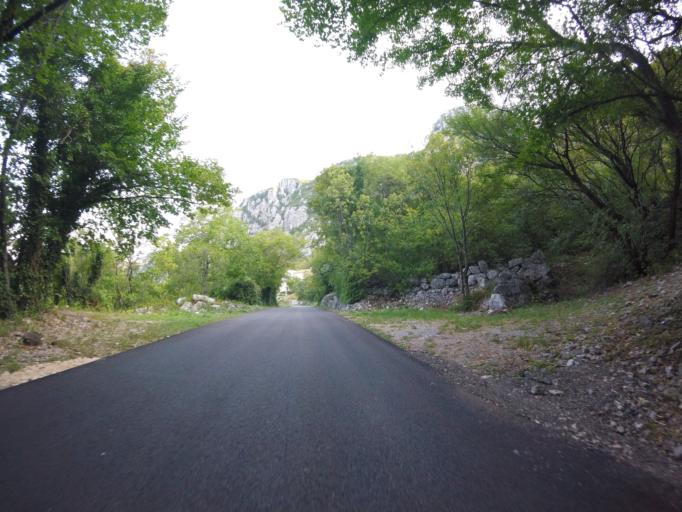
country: HR
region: Primorsko-Goranska
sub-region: Grad Crikvenica
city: Crikvenica
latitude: 45.2139
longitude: 14.7101
